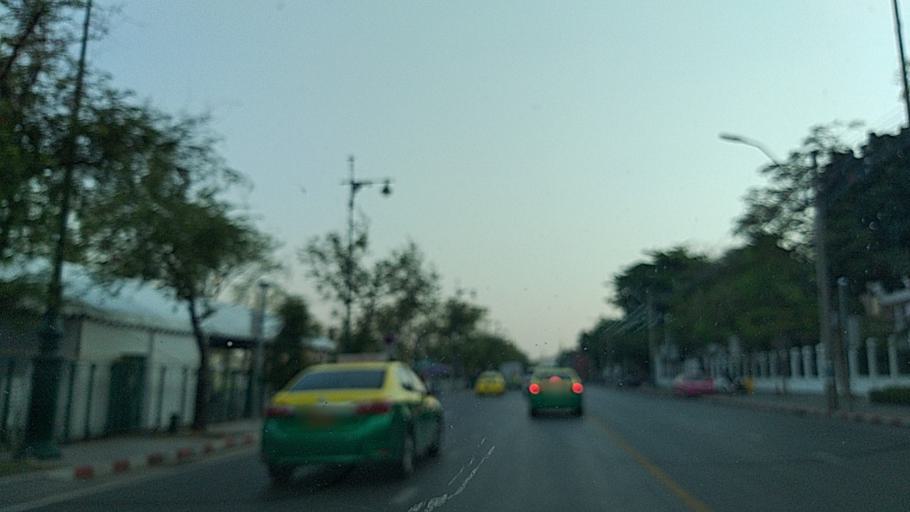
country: TH
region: Bangkok
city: Bangkok
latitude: 13.7566
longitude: 100.4925
